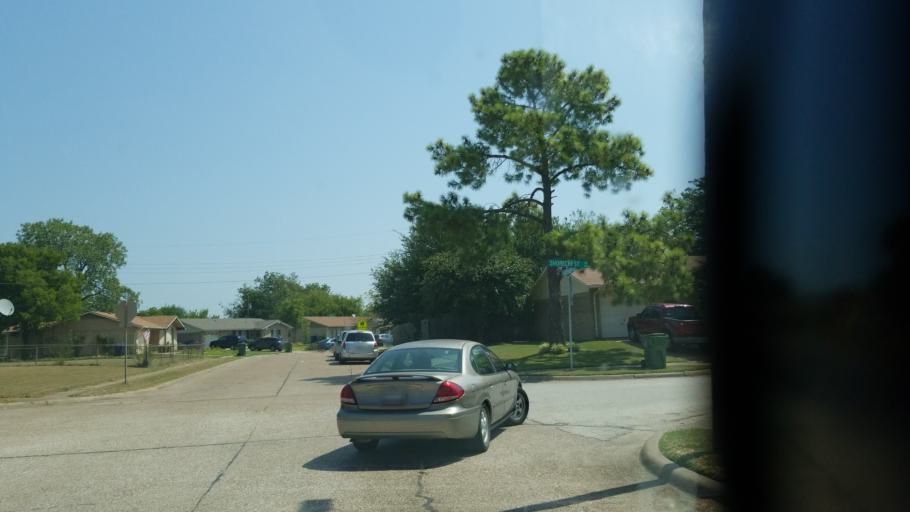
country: US
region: Texas
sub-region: Dallas County
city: Garland
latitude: 32.9171
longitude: -96.6255
